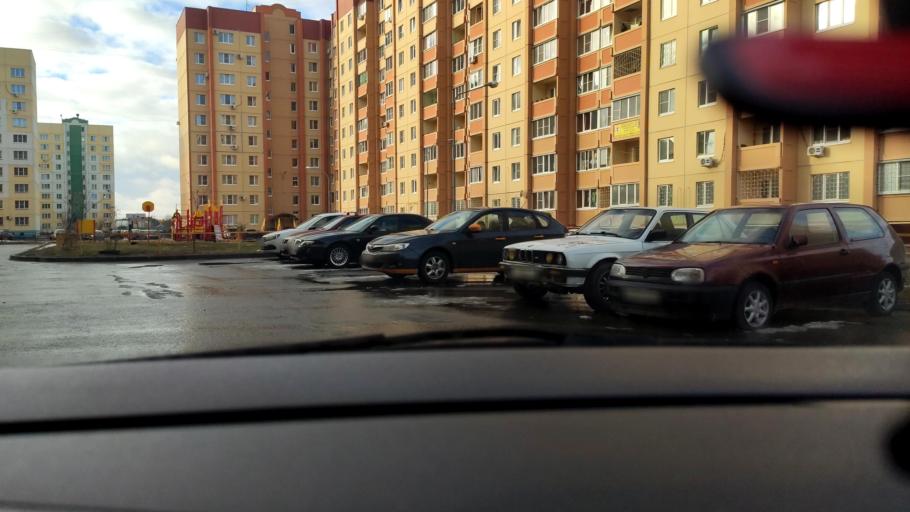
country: RU
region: Voronezj
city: Pridonskoy
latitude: 51.6219
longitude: 39.0638
